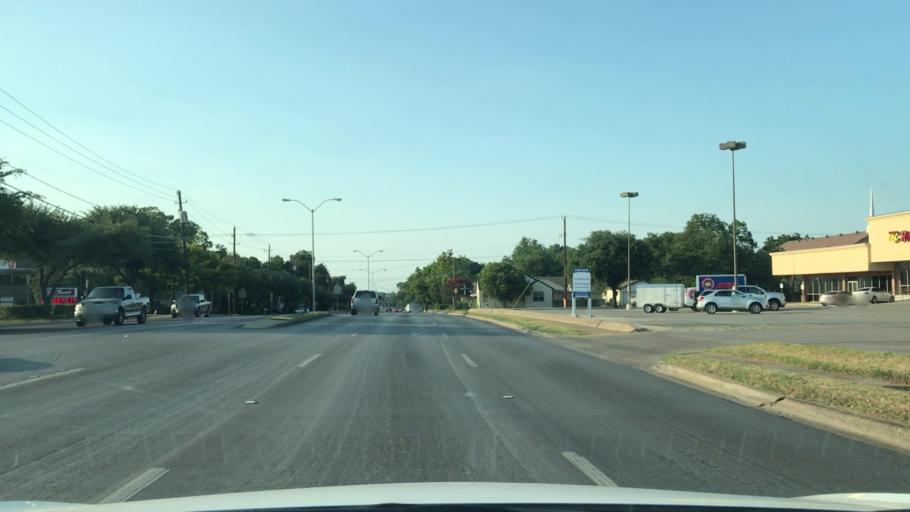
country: US
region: Texas
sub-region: Dallas County
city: Cockrell Hill
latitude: 32.7421
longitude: -96.8567
